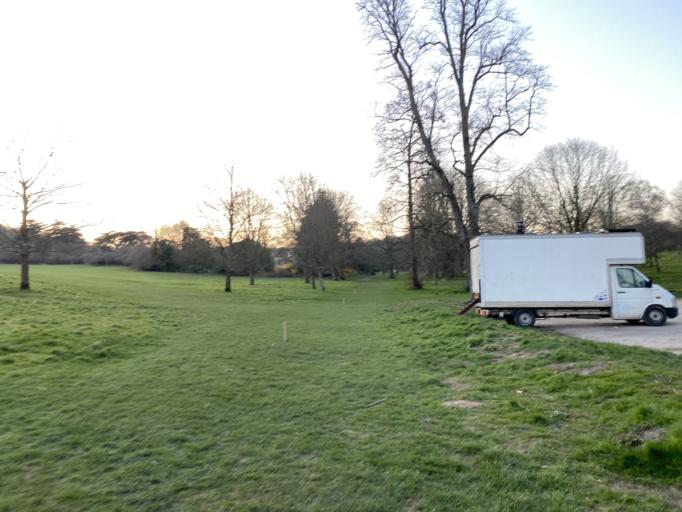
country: GB
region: England
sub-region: Brighton and Hove
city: Brighton
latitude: 50.8679
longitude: -0.0990
